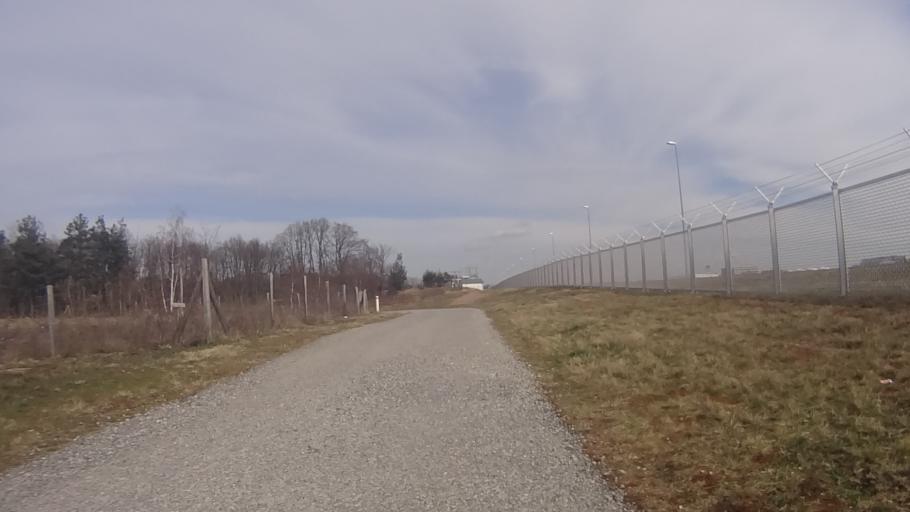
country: DE
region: Hesse
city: Kelsterbach
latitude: 50.0470
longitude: 8.5270
